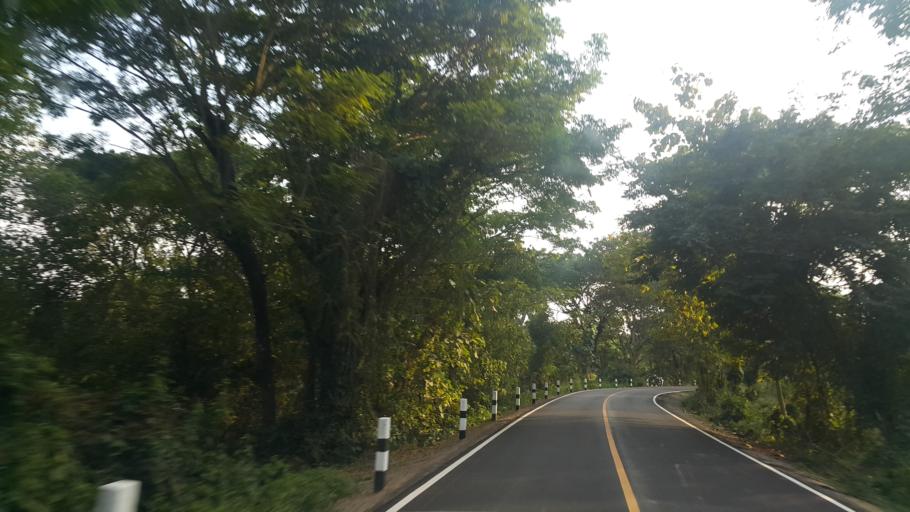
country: TH
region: Lampang
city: Sop Prap
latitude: 17.9354
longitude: 99.3404
